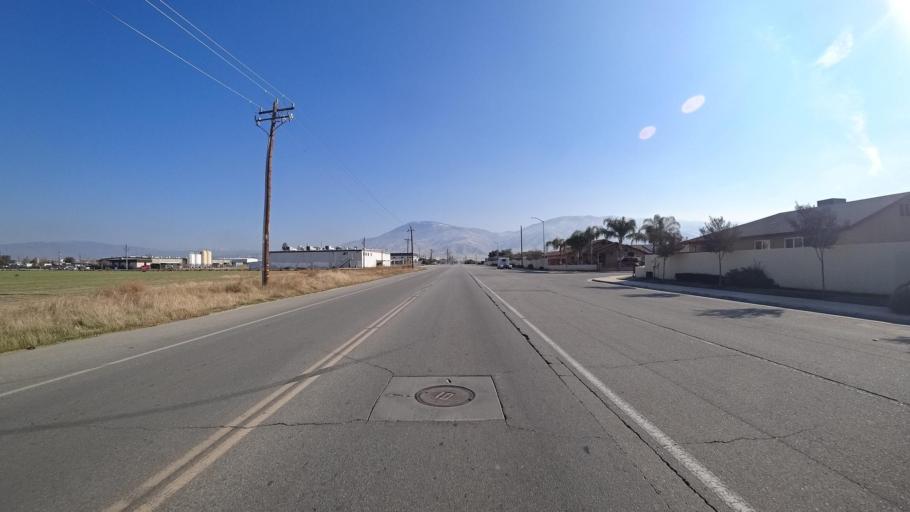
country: US
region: California
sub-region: Kern County
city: Arvin
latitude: 35.1945
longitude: -118.8276
